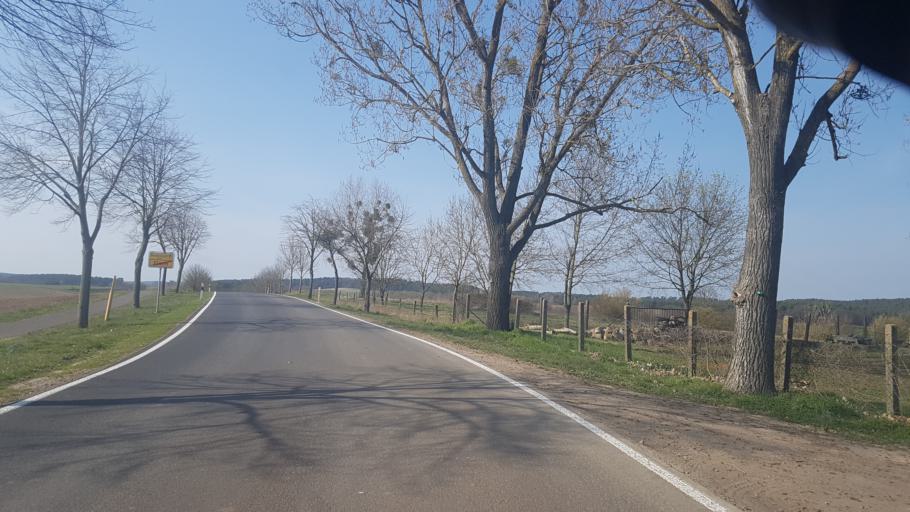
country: DE
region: Brandenburg
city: Gerswalde
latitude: 53.1626
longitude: 13.8127
